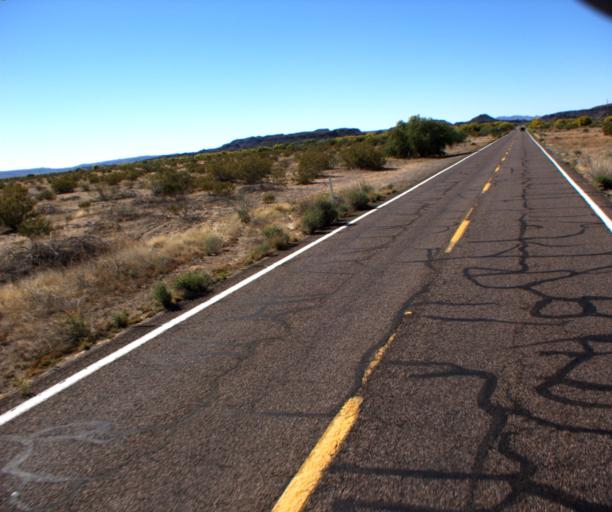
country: US
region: Arizona
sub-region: Pima County
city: Ajo
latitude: 32.5862
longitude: -112.8729
